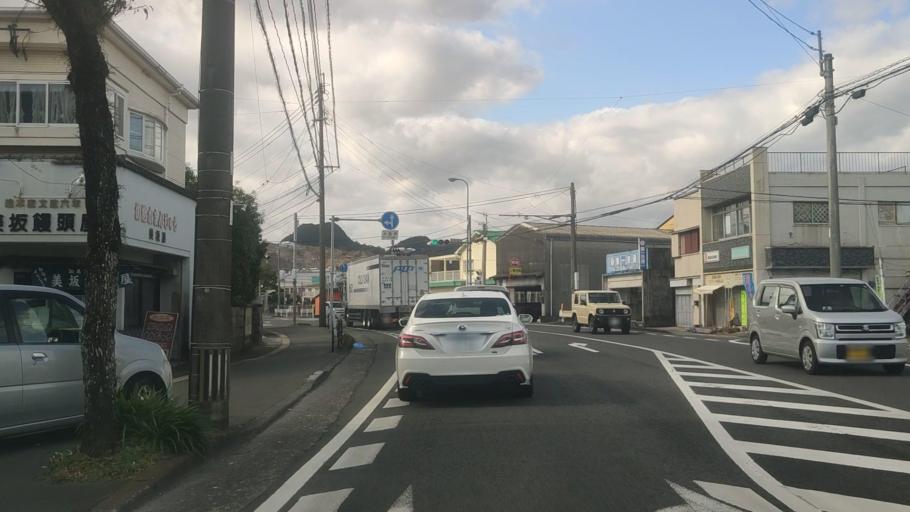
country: JP
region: Kagoshima
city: Kajiki
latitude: 31.7362
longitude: 130.6625
